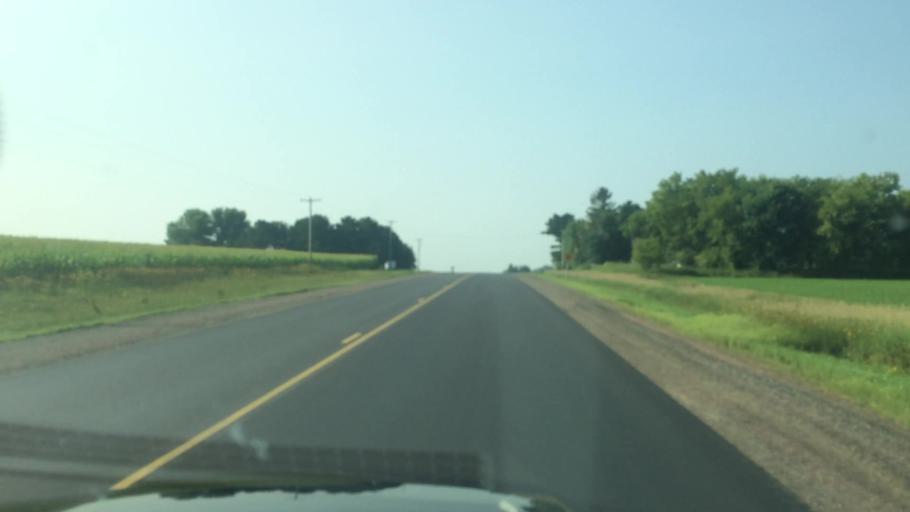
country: US
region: Wisconsin
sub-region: Marathon County
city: Stratford
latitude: 44.8906
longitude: -90.0789
